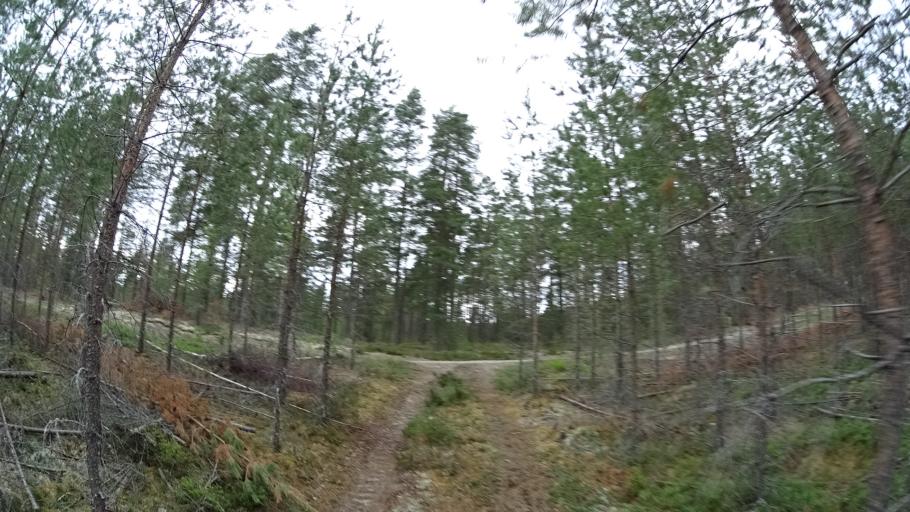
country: FI
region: Satakunta
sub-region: Pohjois-Satakunta
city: Jaemijaervi
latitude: 61.7652
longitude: 22.7604
